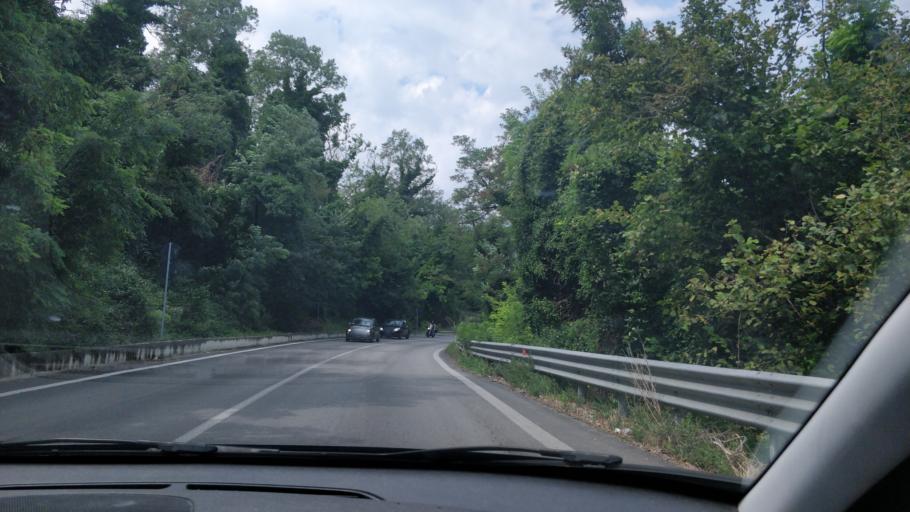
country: IT
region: Abruzzo
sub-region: Provincia di Chieti
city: Marina di San Vito
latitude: 42.3237
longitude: 14.4181
